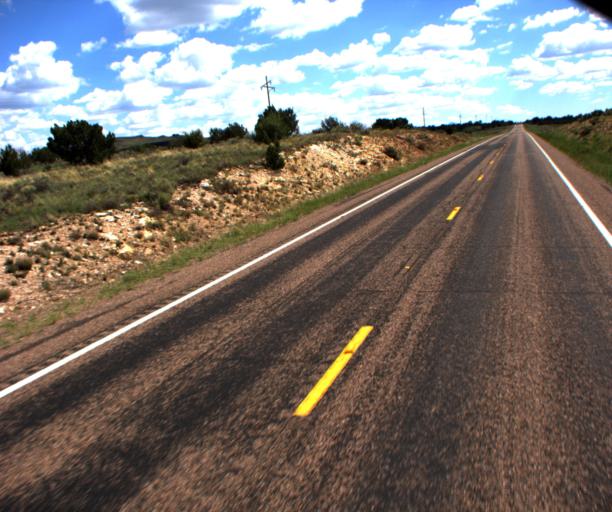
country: US
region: Arizona
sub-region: Coconino County
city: Williams
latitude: 35.5638
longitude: -112.1569
